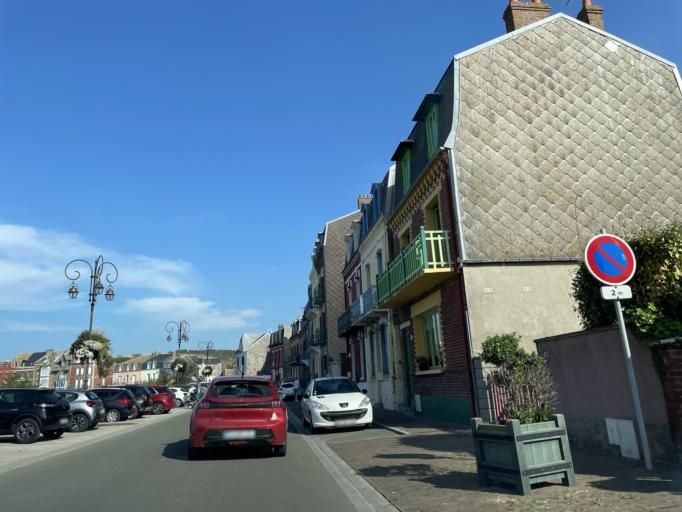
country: FR
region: Picardie
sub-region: Departement de la Somme
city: Mers-les-Bains
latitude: 50.0644
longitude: 1.3859
